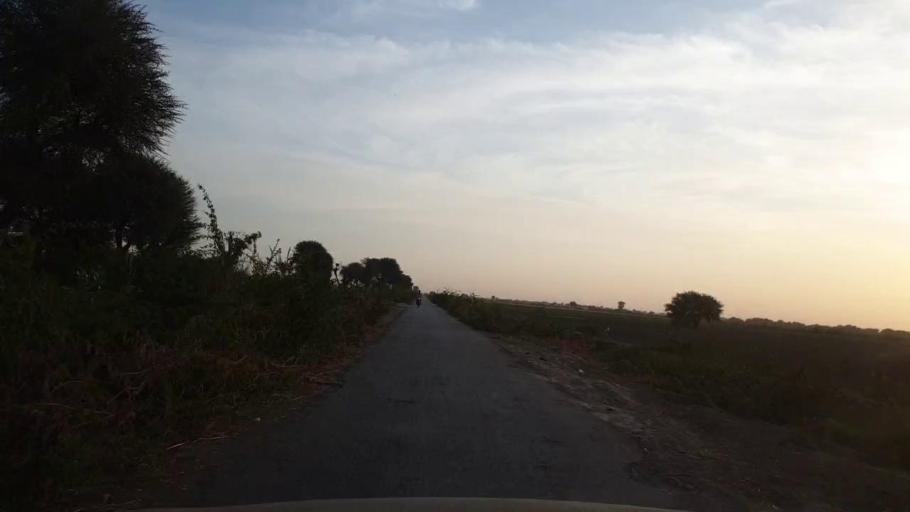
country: PK
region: Sindh
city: Kunri
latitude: 25.1300
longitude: 69.5726
